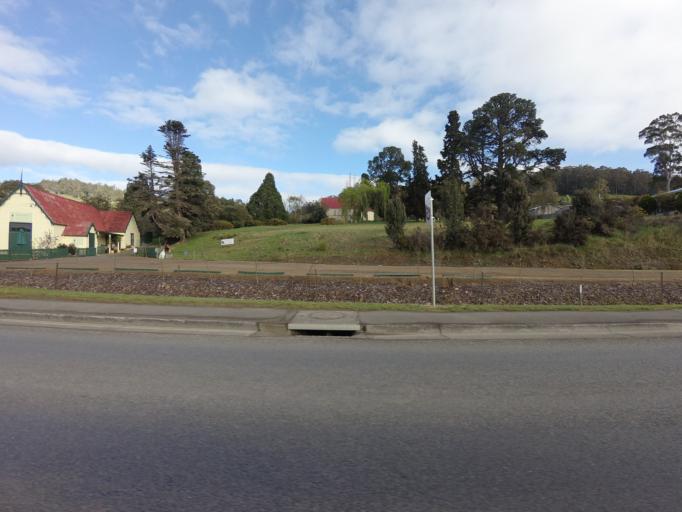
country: AU
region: Tasmania
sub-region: Huon Valley
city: Franklin
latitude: -43.0851
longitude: 147.0142
